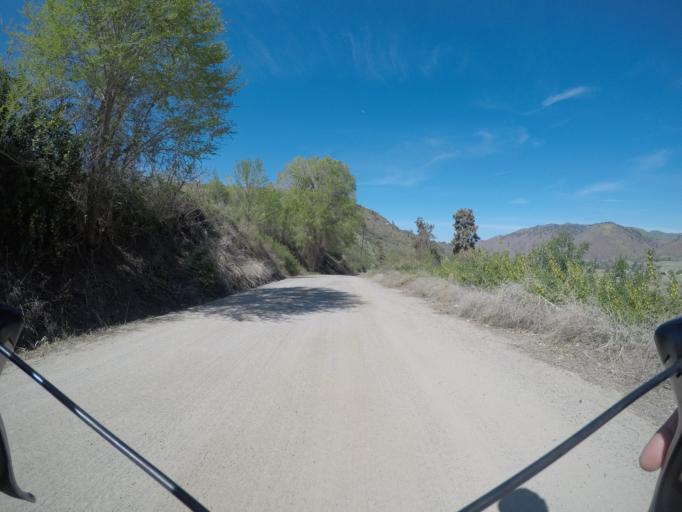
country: US
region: Washington
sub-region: Chelan County
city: Cashmere
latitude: 47.5006
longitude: -120.4380
